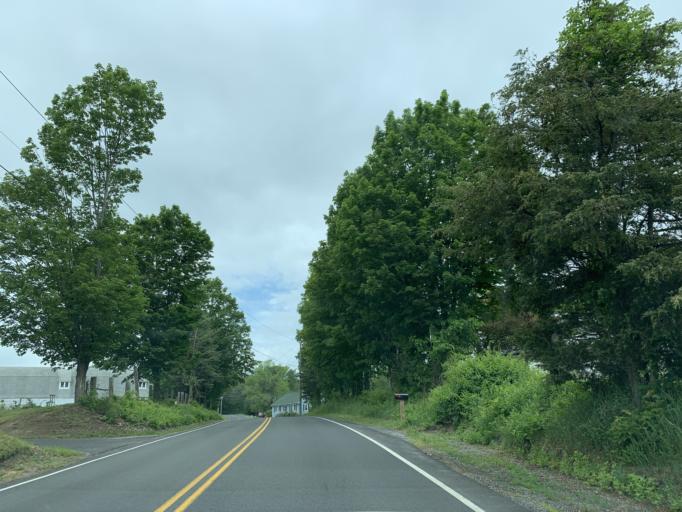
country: US
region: Massachusetts
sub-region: Hampshire County
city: Southampton
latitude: 42.2051
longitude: -72.7987
